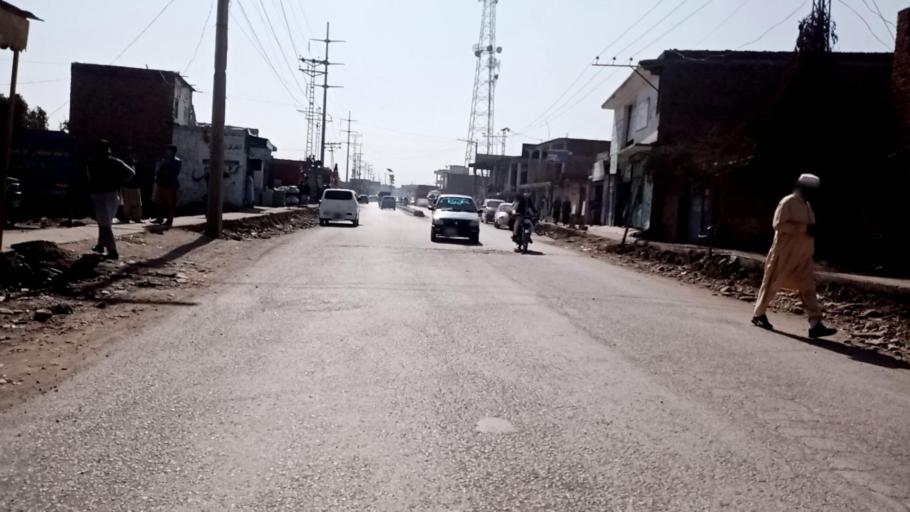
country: PK
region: Khyber Pakhtunkhwa
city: Peshawar
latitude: 33.9186
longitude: 71.4606
